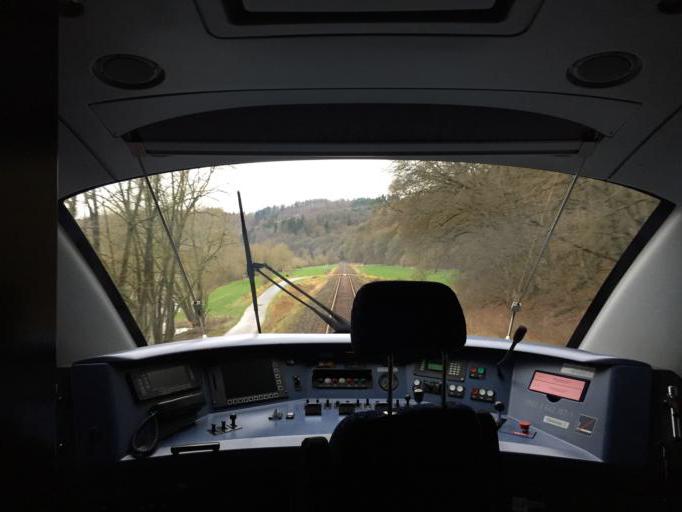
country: DE
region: Hesse
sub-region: Regierungsbezirk Kassel
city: Vohl
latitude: 51.1552
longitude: 8.8960
